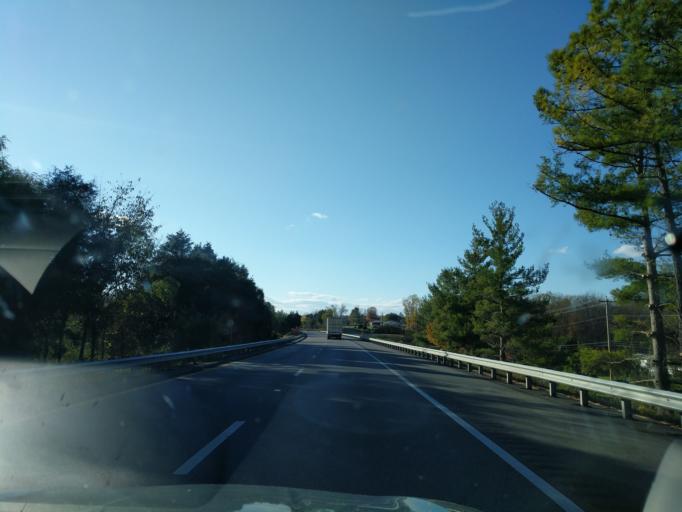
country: US
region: Virginia
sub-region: Smyth County
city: Adwolf
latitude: 36.8128
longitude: -81.5814
